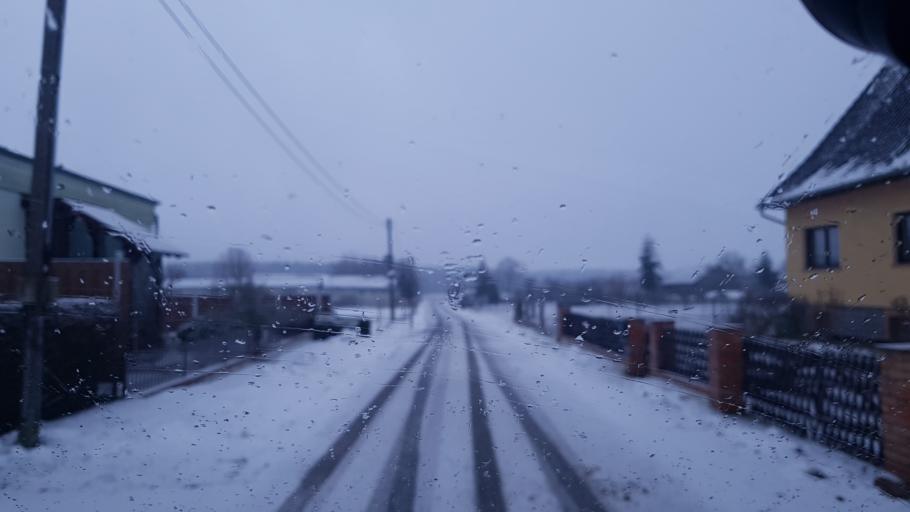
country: DE
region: Brandenburg
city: Janschwalde
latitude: 51.8967
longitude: 14.5164
